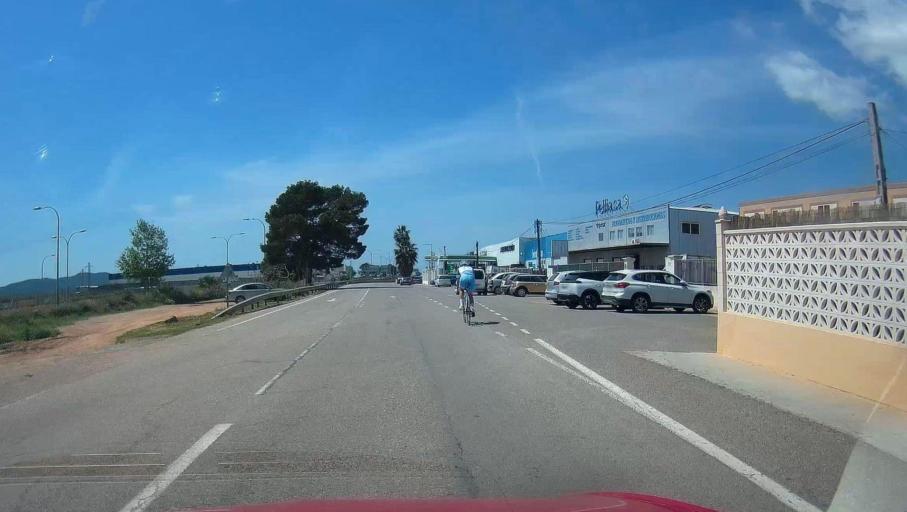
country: ES
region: Balearic Islands
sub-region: Illes Balears
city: Ibiza
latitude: 38.8868
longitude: 1.3935
